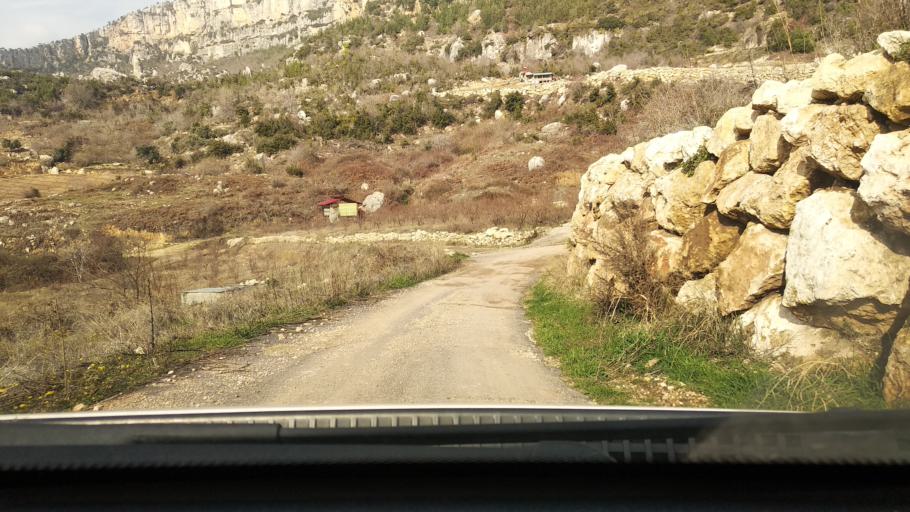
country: TR
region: Mersin
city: Kuzucubelen
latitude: 36.8766
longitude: 34.4730
